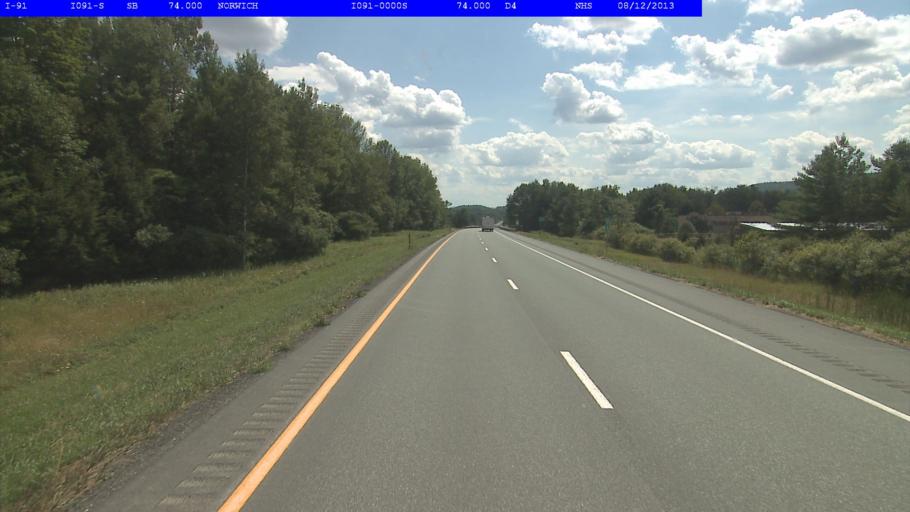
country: US
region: Vermont
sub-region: Windsor County
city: Wilder
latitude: 43.6946
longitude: -72.3112
